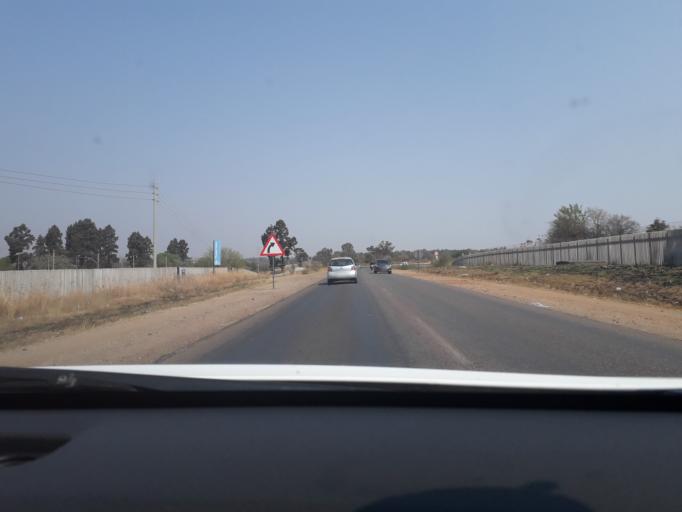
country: ZA
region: Gauteng
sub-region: City of Tshwane Metropolitan Municipality
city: Centurion
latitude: -25.9137
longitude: 28.2282
